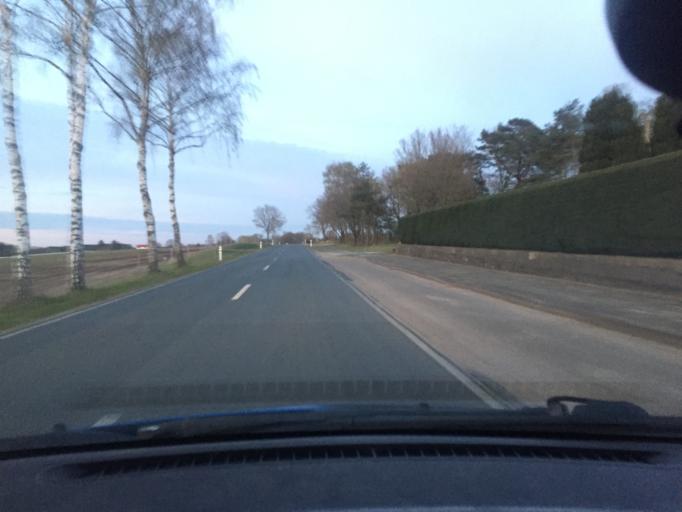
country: DE
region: Lower Saxony
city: Handeloh
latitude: 53.2665
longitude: 9.8980
